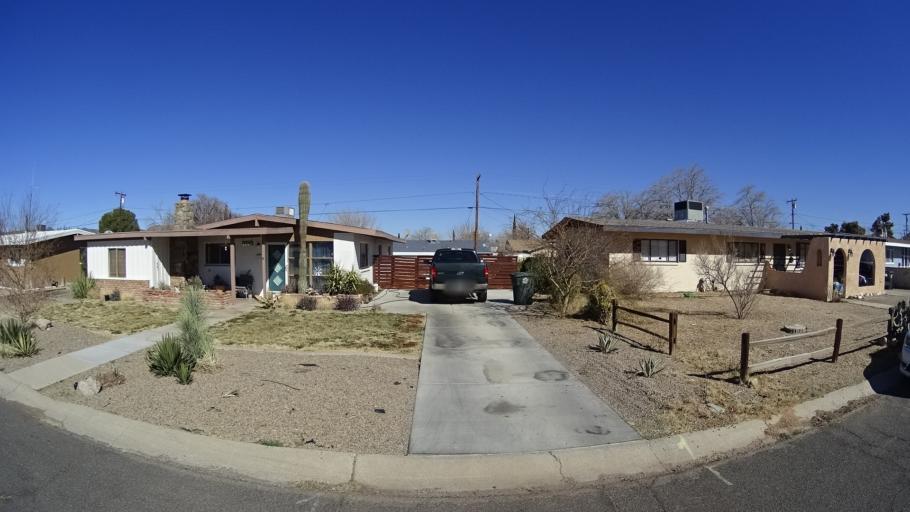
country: US
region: Arizona
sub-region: Mohave County
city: Kingman
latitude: 35.2110
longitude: -114.0210
